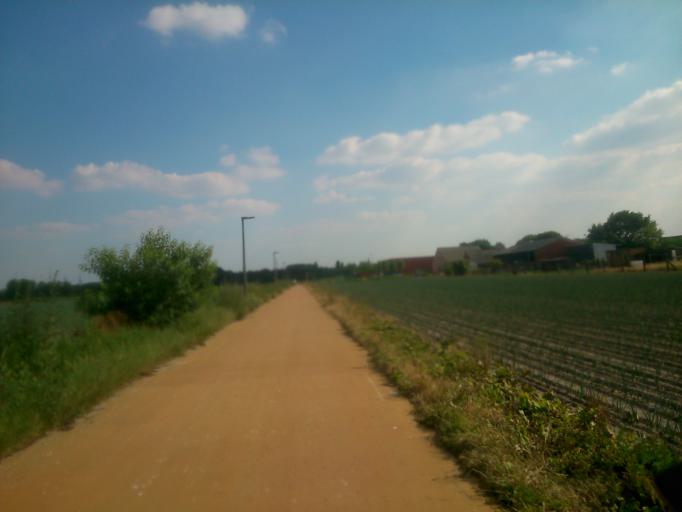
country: BE
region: Flanders
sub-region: Provincie Antwerpen
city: Stabroek
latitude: 51.3519
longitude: 4.3165
